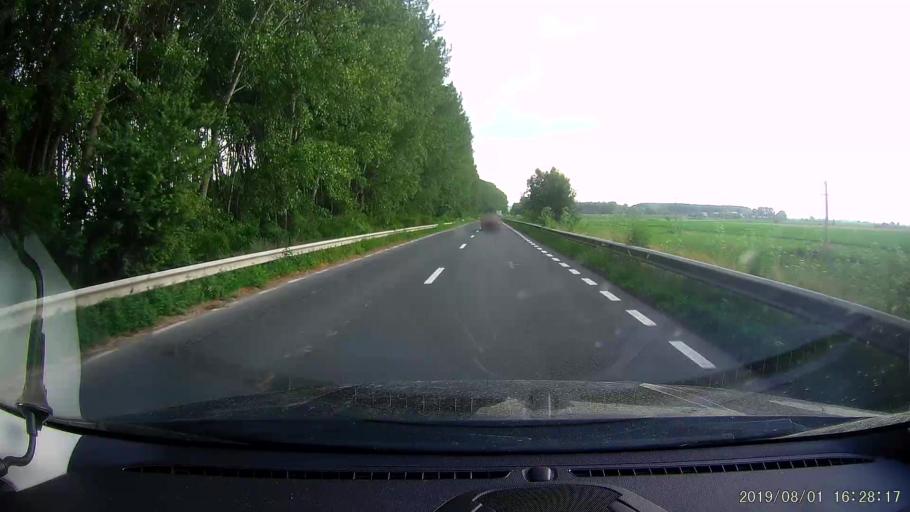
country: BG
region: Silistra
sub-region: Obshtina Silistra
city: Silistra
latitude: 44.1498
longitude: 27.3108
